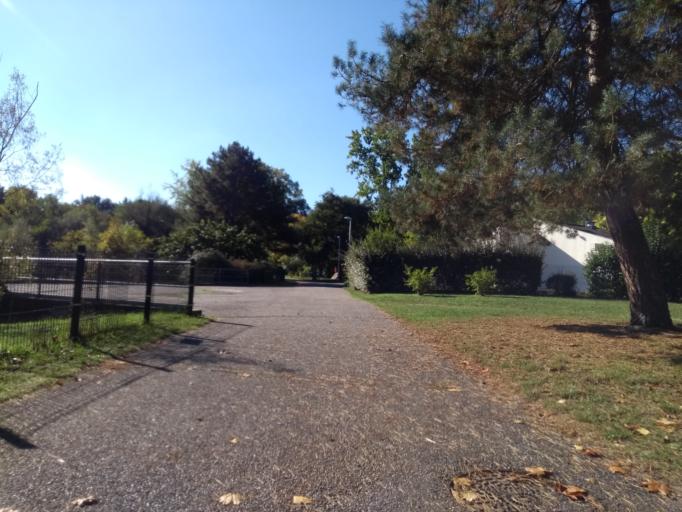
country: FR
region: Aquitaine
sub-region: Departement de la Gironde
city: Pessac
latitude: 44.7977
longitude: -0.6273
